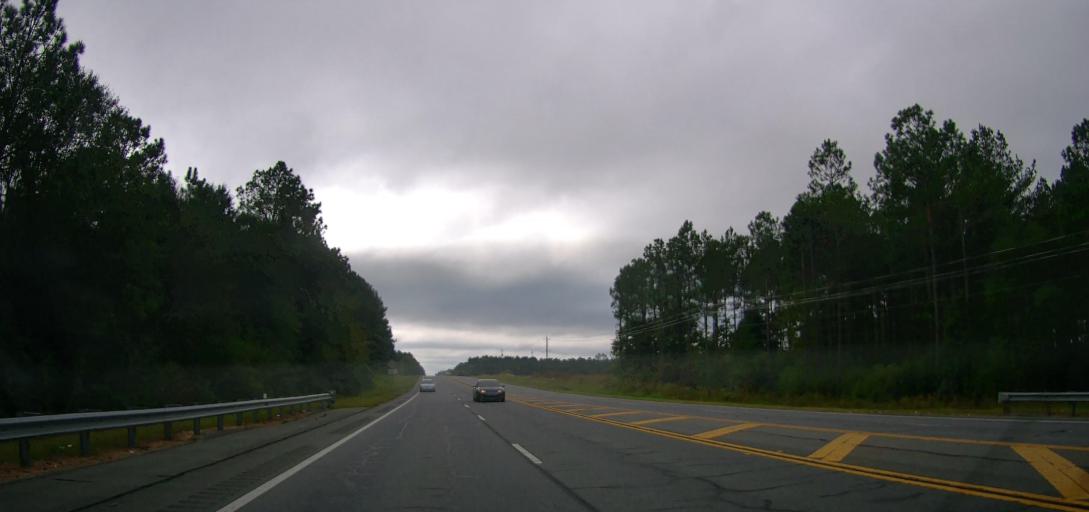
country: US
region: Georgia
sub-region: Colquitt County
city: Moultrie
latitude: 31.2399
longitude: -83.7320
